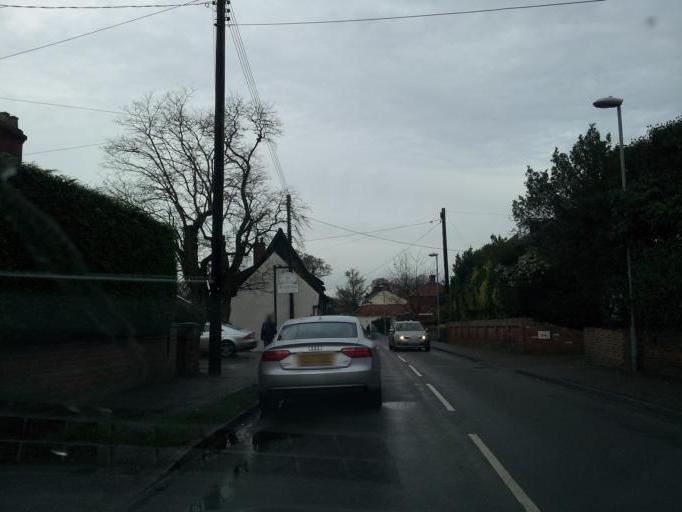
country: GB
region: England
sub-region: Norfolk
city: Brundall
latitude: 52.6238
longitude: 1.4359
